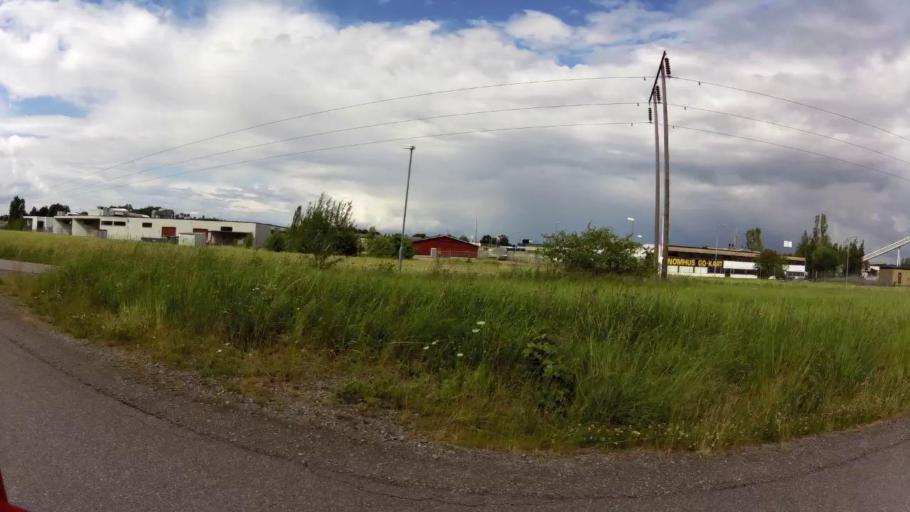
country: SE
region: OEstergoetland
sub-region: Linkopings Kommun
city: Linkoping
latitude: 58.3964
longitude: 15.6876
